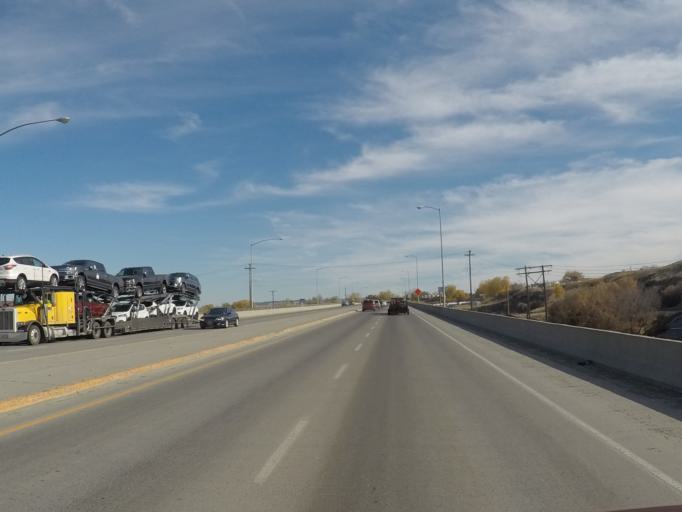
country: US
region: Montana
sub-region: Yellowstone County
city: Billings
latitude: 45.7964
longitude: -108.4704
